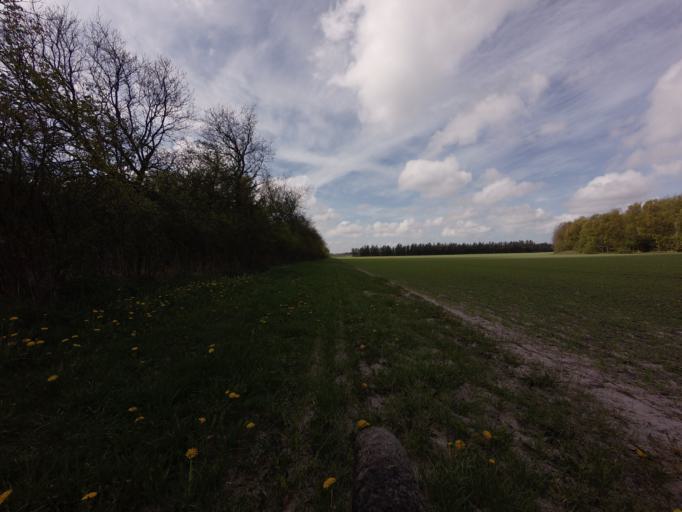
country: DK
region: North Denmark
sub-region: Jammerbugt Kommune
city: Kas
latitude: 57.1977
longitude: 9.6212
